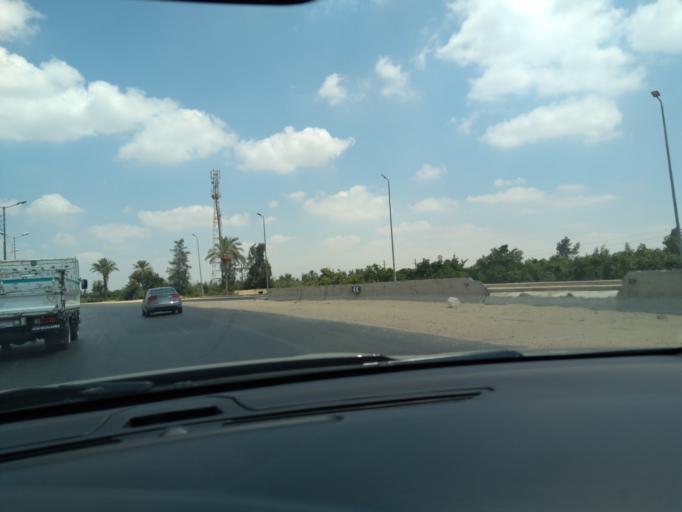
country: EG
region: Al Isma'iliyah
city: Ismailia
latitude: 30.6682
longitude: 32.2719
